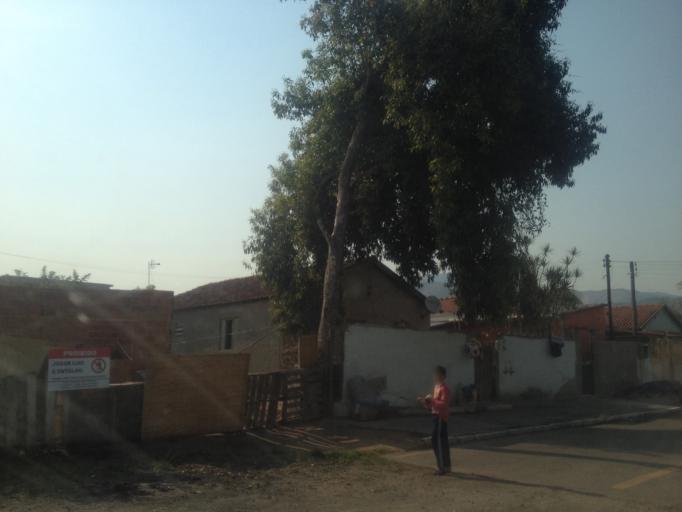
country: BR
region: Rio de Janeiro
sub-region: Porto Real
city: Porto Real
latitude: -22.4634
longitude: -44.3570
